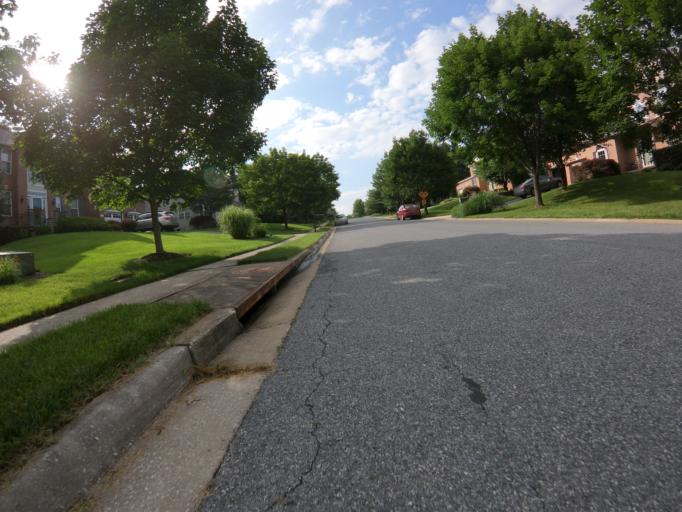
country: US
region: Maryland
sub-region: Howard County
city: Ellicott City
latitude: 39.2490
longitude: -76.7885
